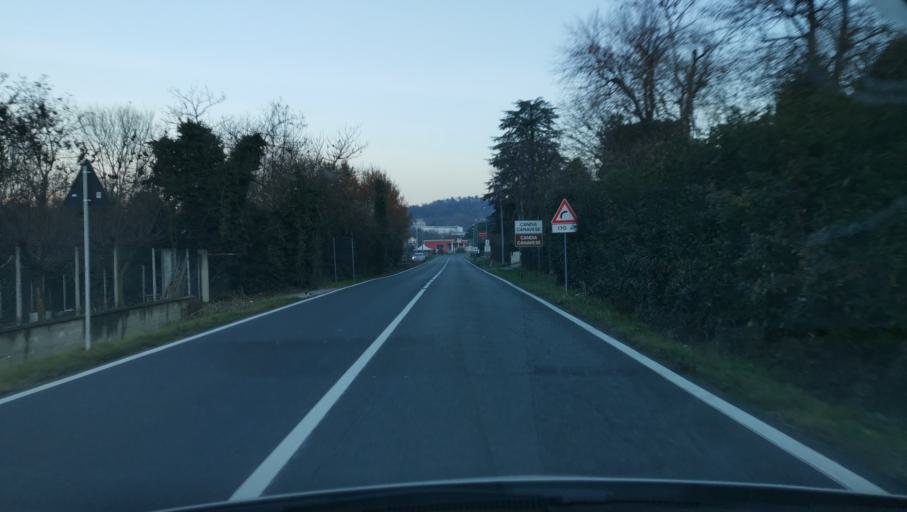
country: IT
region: Piedmont
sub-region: Provincia di Torino
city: Barone Canavese
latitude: 45.3184
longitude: 7.8787
